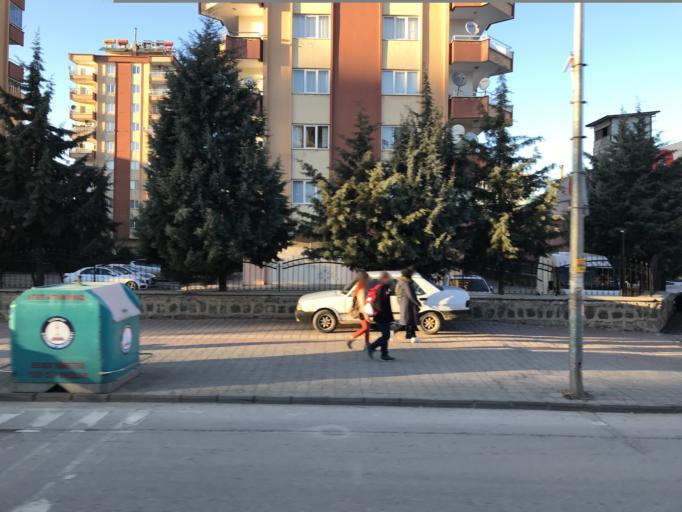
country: TR
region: Gaziantep
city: Sahinbey
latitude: 37.0154
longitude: 37.3514
